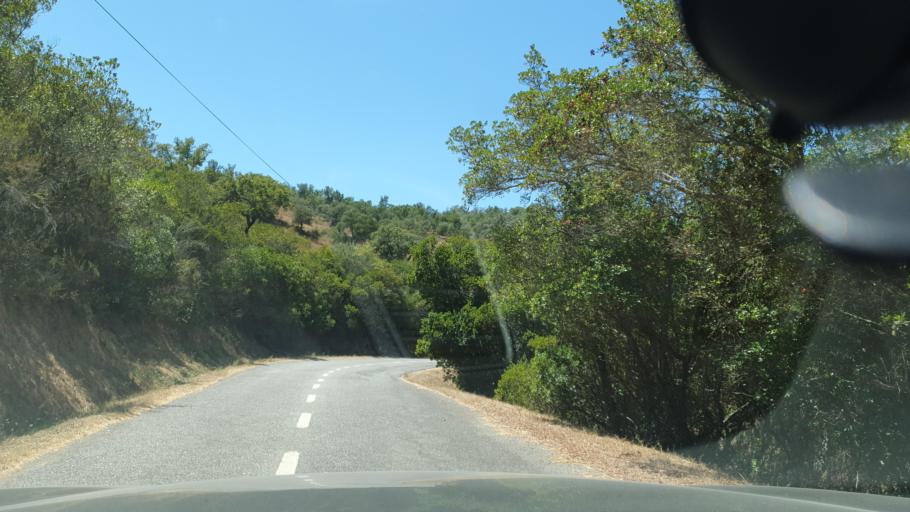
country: PT
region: Beja
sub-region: Odemira
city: Odemira
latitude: 37.6038
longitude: -8.5766
